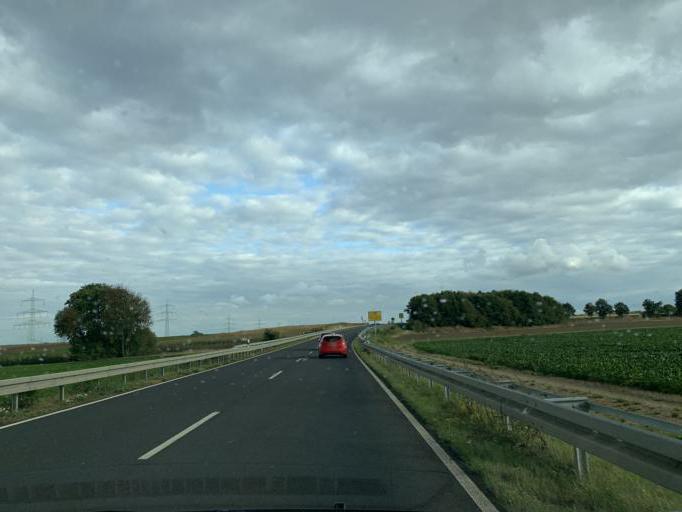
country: DE
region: North Rhine-Westphalia
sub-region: Regierungsbezirk Koln
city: Aldenhoven
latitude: 50.9239
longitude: 6.3065
